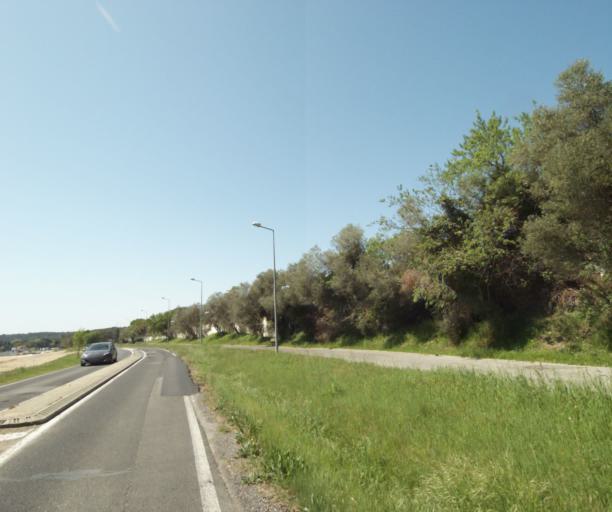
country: FR
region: Languedoc-Roussillon
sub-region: Departement de l'Herault
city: Clapiers
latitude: 43.6576
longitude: 3.8941
